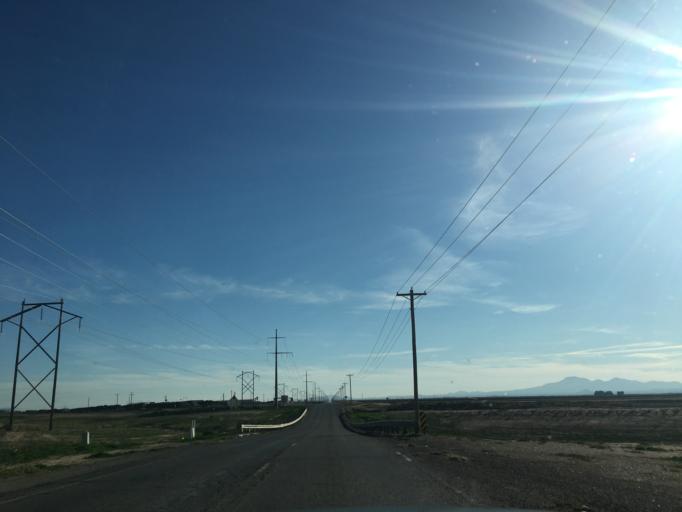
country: US
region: Arizona
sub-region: Pinal County
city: Maricopa
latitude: 33.0173
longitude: -111.9966
